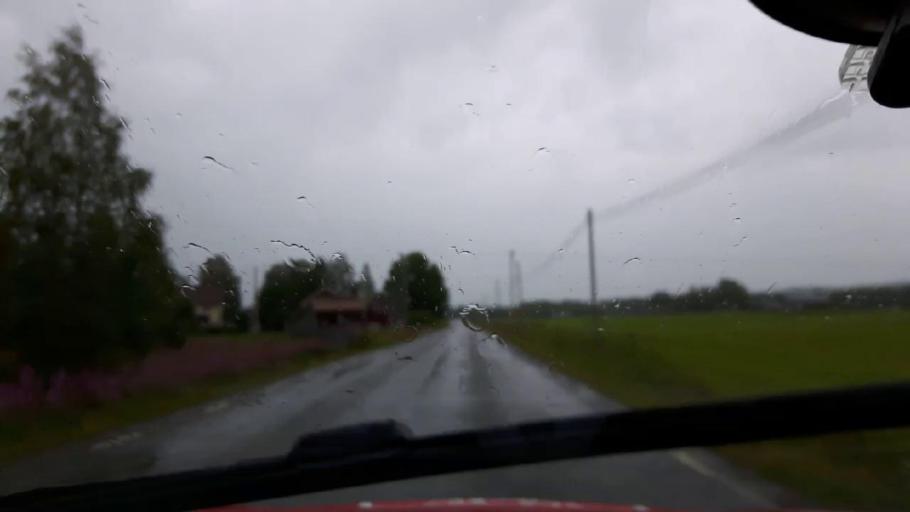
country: SE
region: Jaemtland
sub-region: OEstersunds Kommun
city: Brunflo
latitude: 62.9947
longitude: 14.7847
